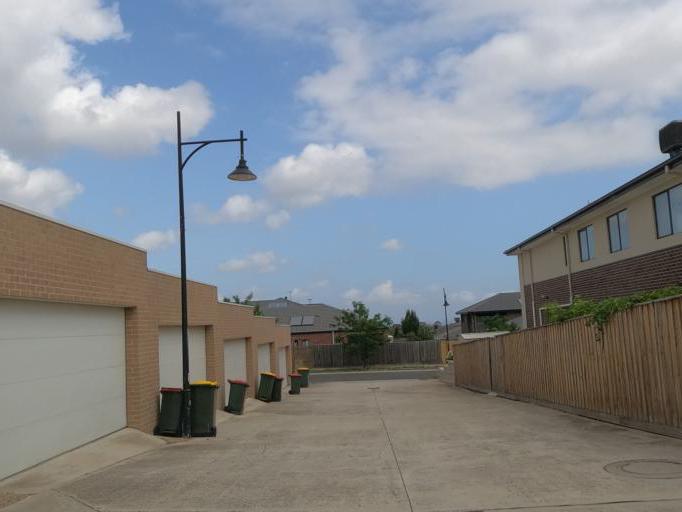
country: AU
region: Victoria
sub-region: Hume
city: Greenvale
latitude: -37.6234
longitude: 144.8915
